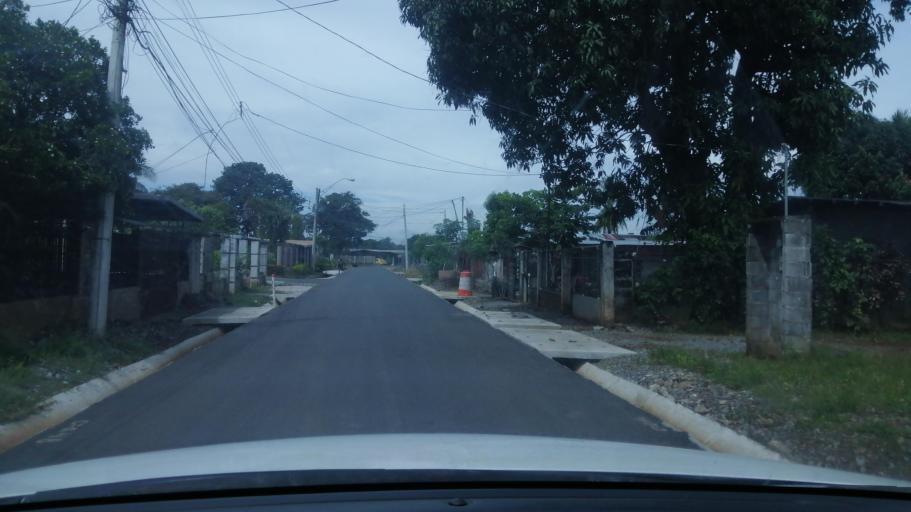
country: PA
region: Chiriqui
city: David
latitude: 8.4172
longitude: -82.4502
